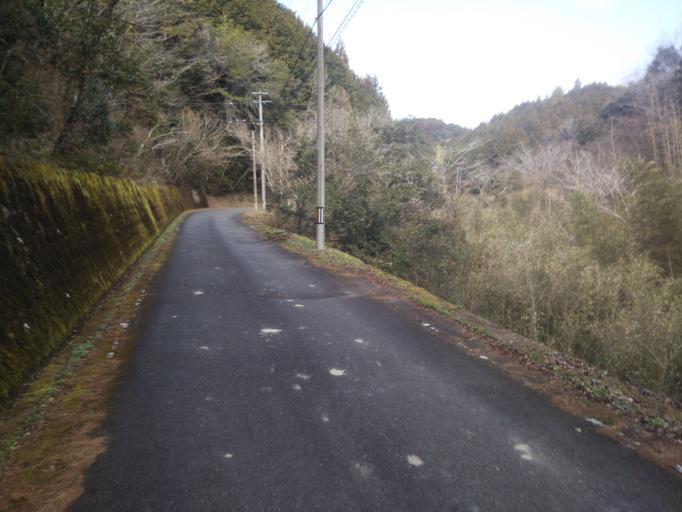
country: JP
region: Kochi
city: Nakamura
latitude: 33.0358
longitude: 132.9850
